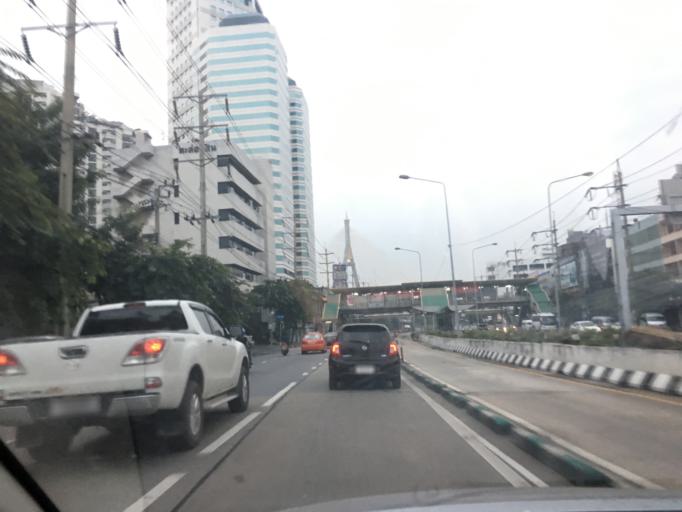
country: TH
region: Samut Prakan
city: Phra Pradaeng
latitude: 13.6749
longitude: 100.5443
